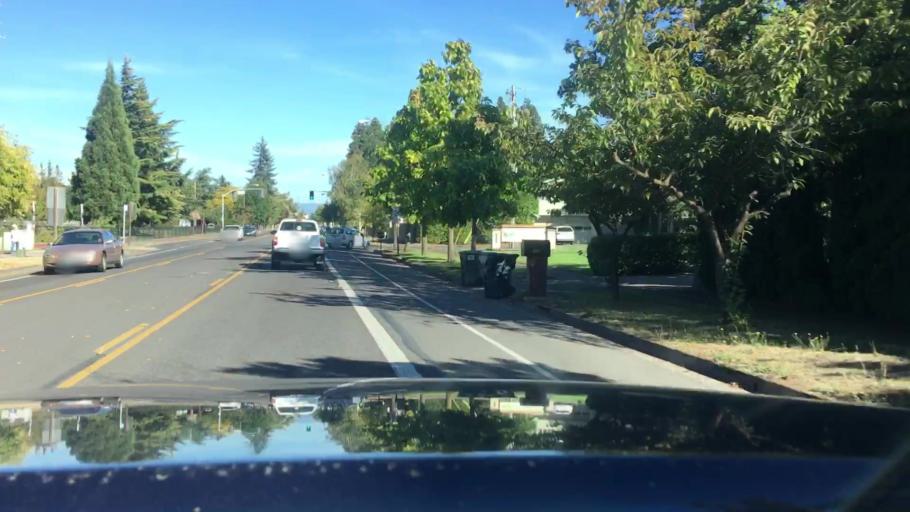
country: US
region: Oregon
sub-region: Lane County
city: Eugene
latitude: 44.0697
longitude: -123.0569
